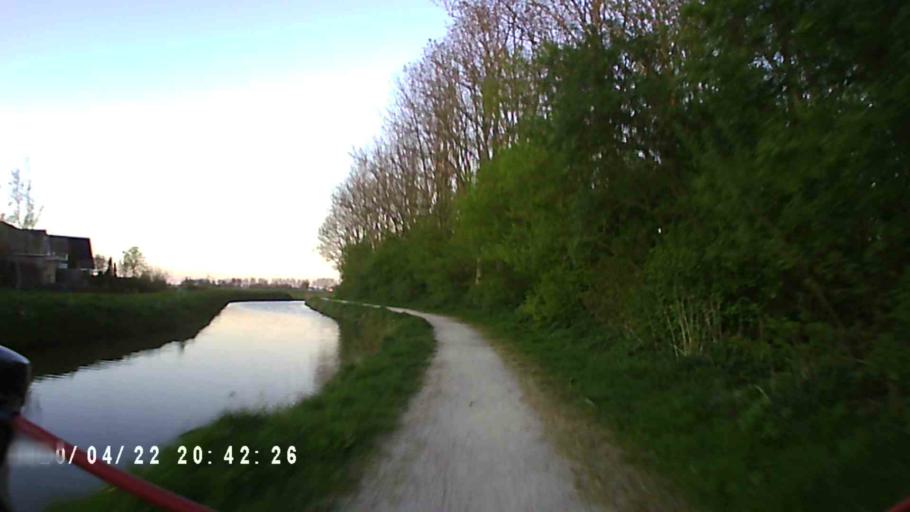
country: NL
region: Groningen
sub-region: Gemeente Winsum
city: Winsum
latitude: 53.3254
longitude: 6.5342
